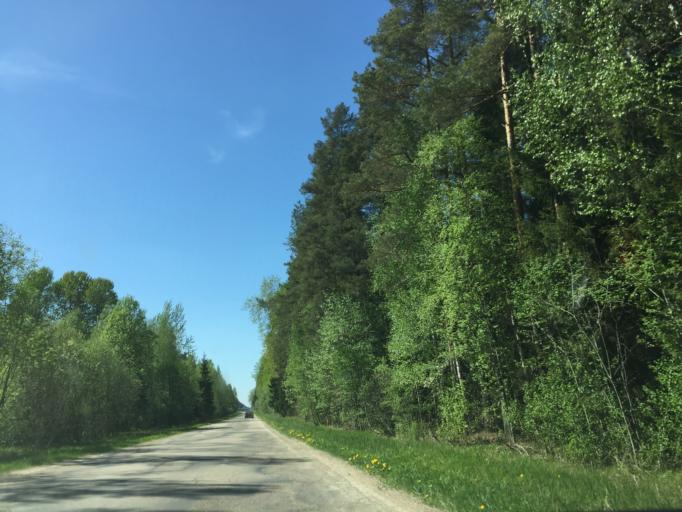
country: LV
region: Ogre
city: Ogre
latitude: 56.8520
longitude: 24.6893
